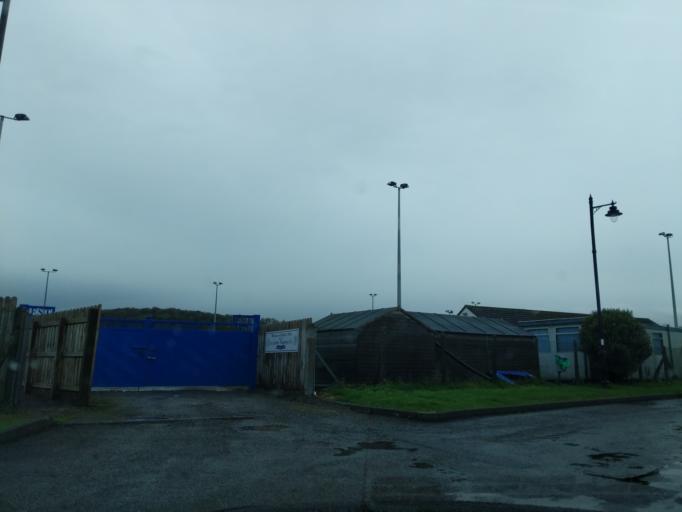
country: GB
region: Scotland
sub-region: Dumfries and Galloway
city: Kirkcudbright
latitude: 54.8331
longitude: -4.0597
